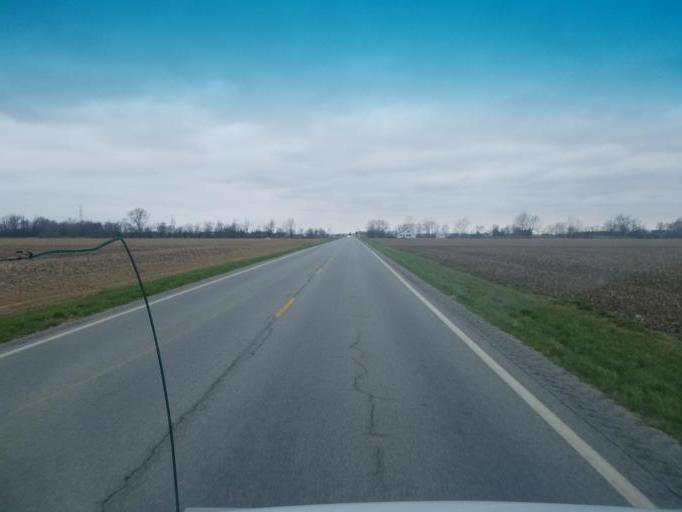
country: US
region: Ohio
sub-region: Allen County
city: Delphos
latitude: 40.9320
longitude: -84.4403
